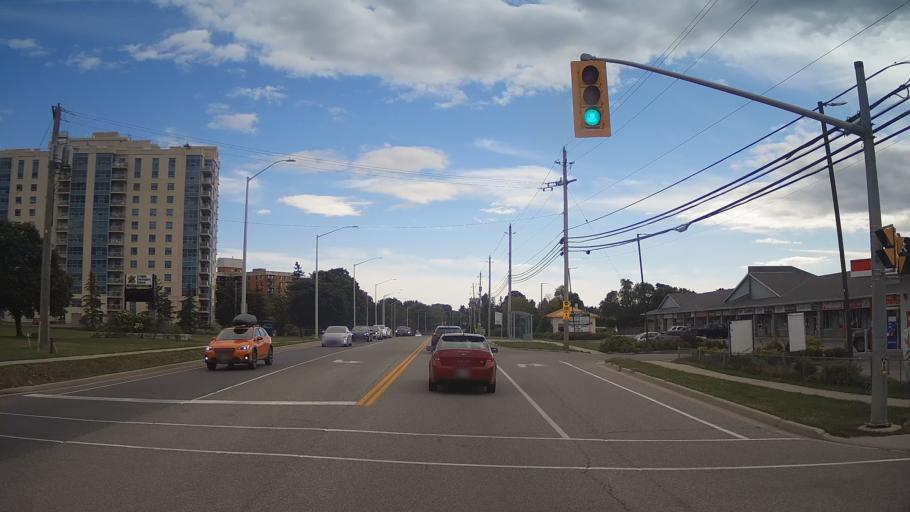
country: CA
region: Ontario
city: Kingston
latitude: 44.2537
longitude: -76.4606
